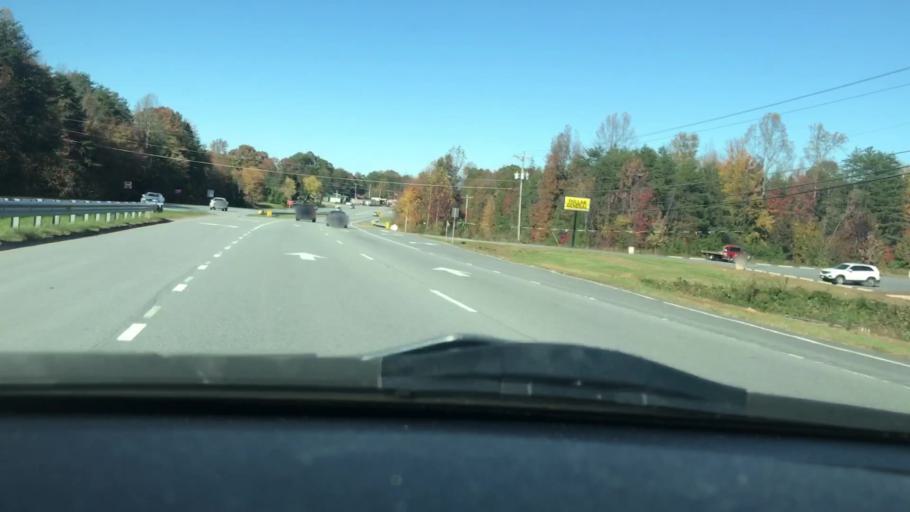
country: US
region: North Carolina
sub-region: Rockingham County
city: Madison
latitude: 36.3276
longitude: -79.9466
